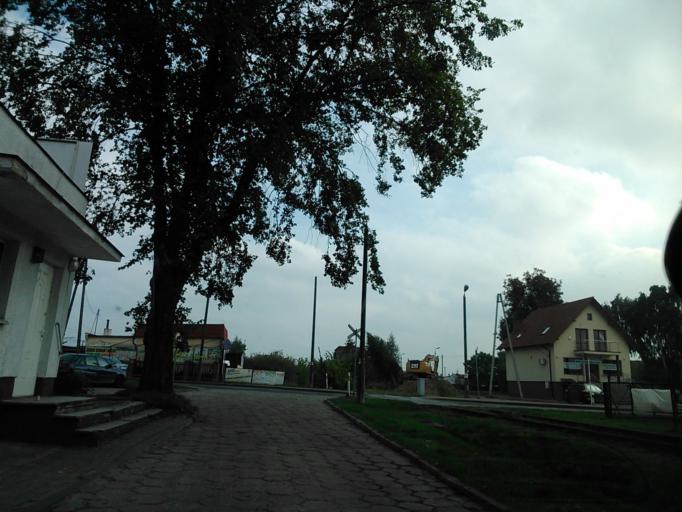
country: PL
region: Kujawsko-Pomorskie
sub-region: Powiat golubsko-dobrzynski
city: Kowalewo Pomorskie
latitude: 53.1579
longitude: 18.9037
